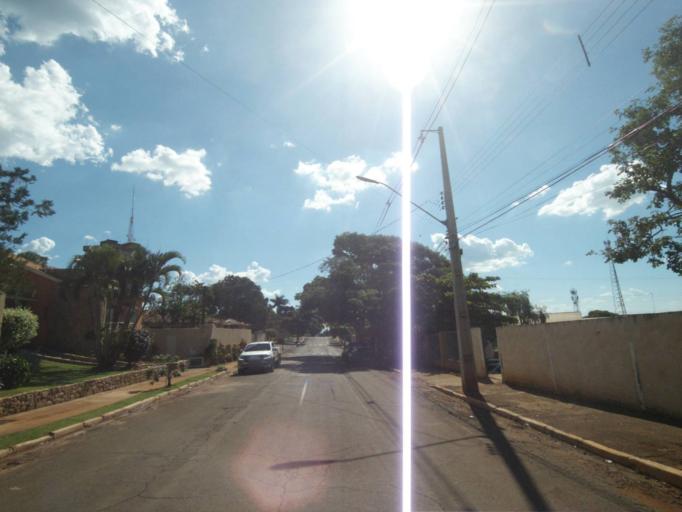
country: BR
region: Parana
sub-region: Sertanopolis
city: Sertanopolis
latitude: -23.0407
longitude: -50.8143
